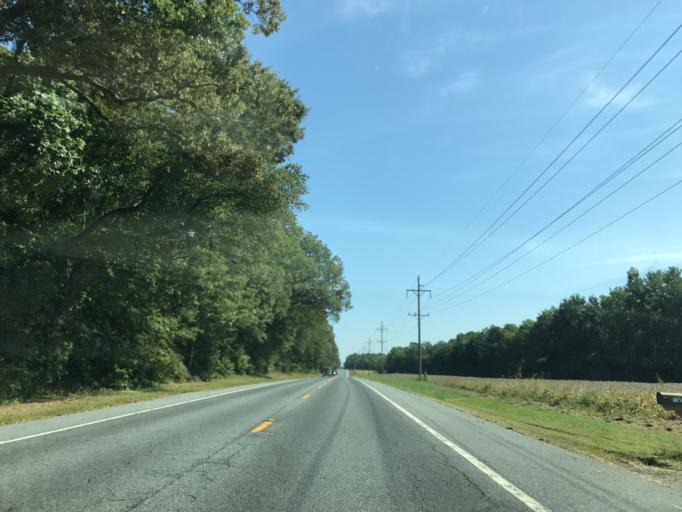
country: US
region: Maryland
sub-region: Queen Anne's County
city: Kingstown
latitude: 39.2632
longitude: -75.9005
